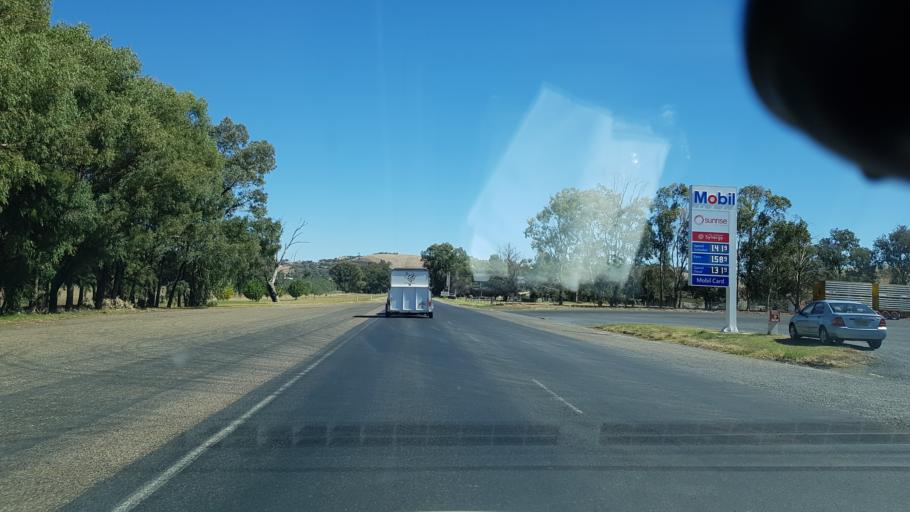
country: AU
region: New South Wales
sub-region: Gundagai
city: Gundagai
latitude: -34.8225
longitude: 148.3431
